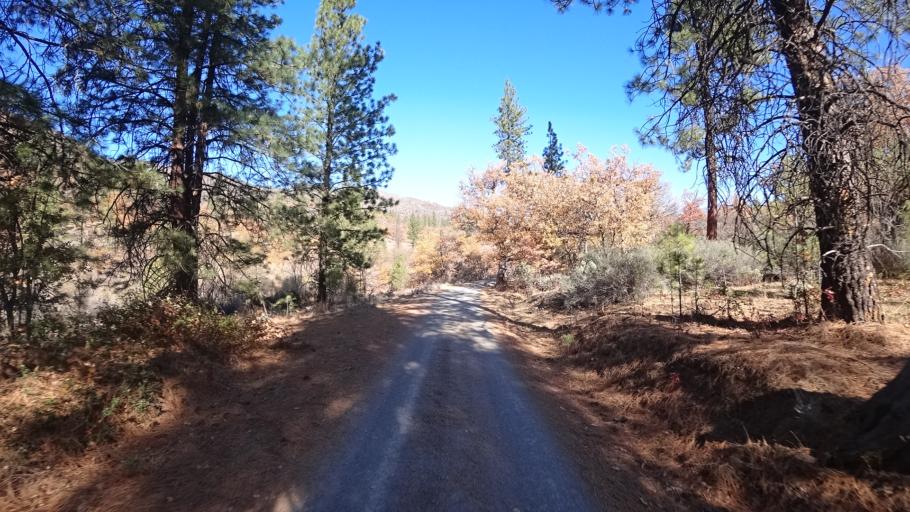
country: US
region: California
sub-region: Siskiyou County
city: Yreka
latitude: 41.8475
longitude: -122.8362
